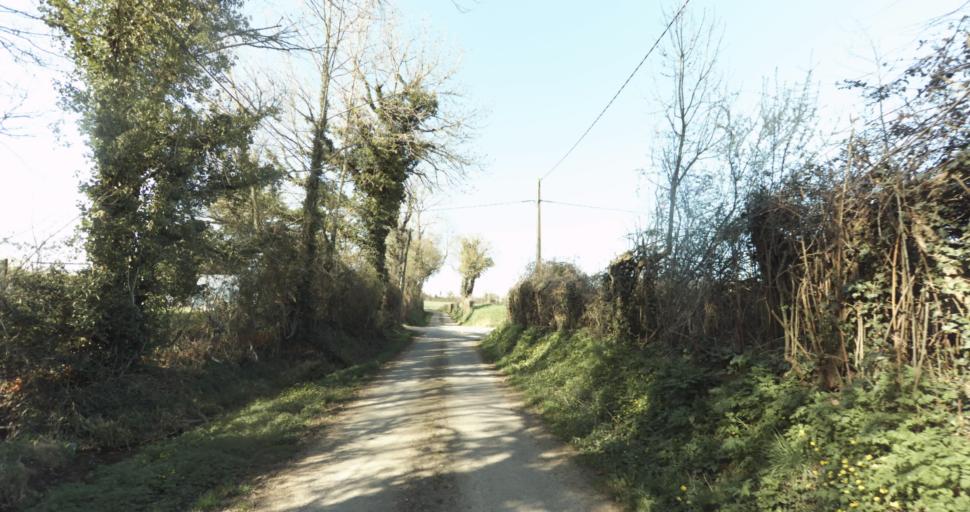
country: FR
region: Lower Normandy
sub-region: Departement du Calvados
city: Saint-Pierre-sur-Dives
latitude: 48.9363
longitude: 0.0043
